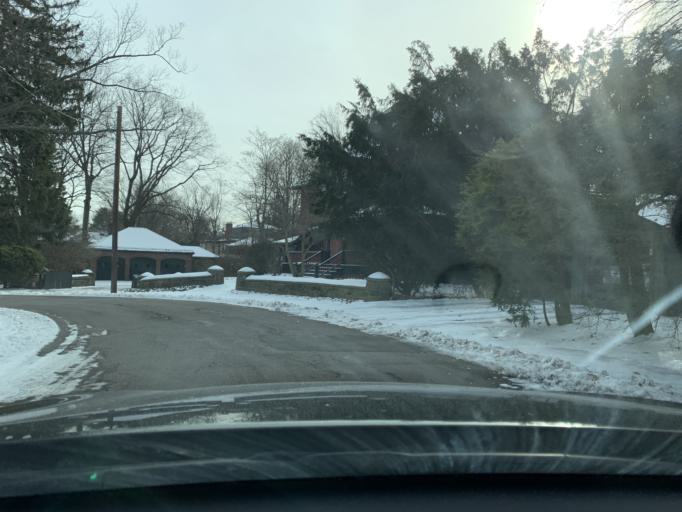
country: US
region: Massachusetts
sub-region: Norfolk County
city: Brookline
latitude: 42.3284
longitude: -71.1207
